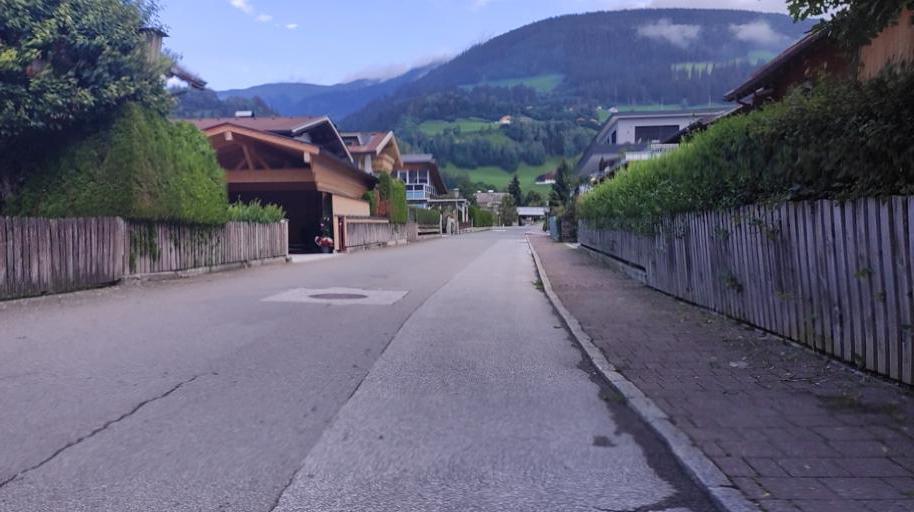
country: AT
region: Salzburg
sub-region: Politischer Bezirk Zell am See
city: Bramberg am Wildkogel
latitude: 47.2754
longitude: 12.3749
